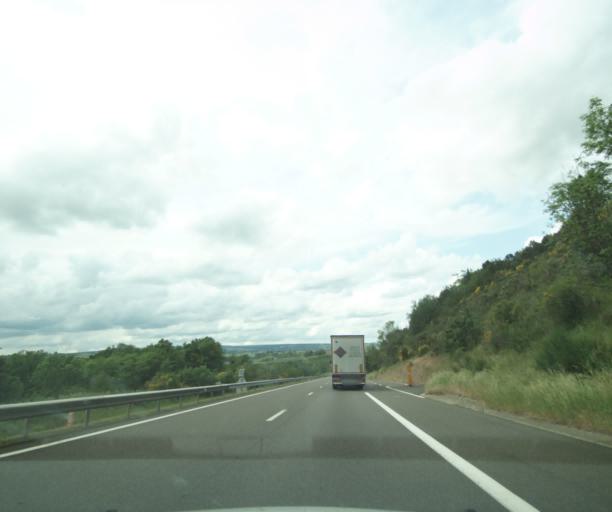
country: FR
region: Auvergne
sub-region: Departement de l'Allier
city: Ebreuil
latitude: 46.1177
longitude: 3.1251
